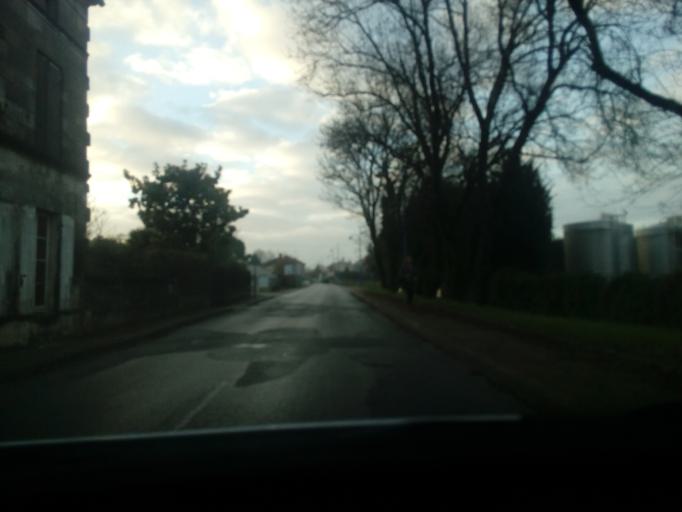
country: FR
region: Poitou-Charentes
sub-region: Departement de la Charente-Maritime
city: Jonzac
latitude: 45.4454
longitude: -0.4267
